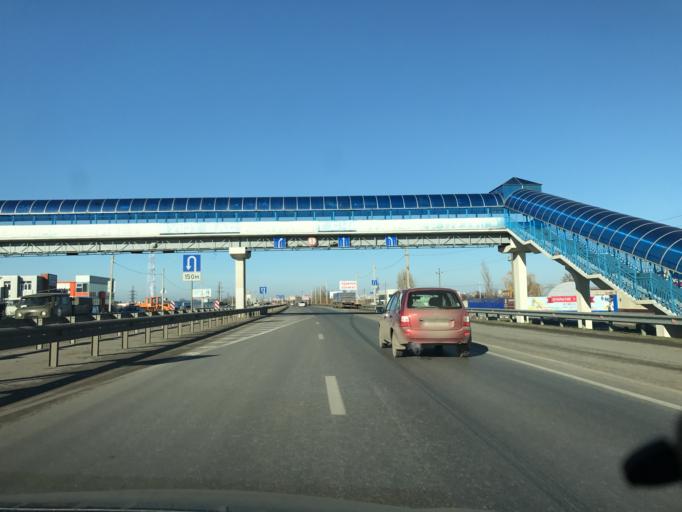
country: RU
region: Rostov
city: Bataysk
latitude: 47.1544
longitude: 39.7703
